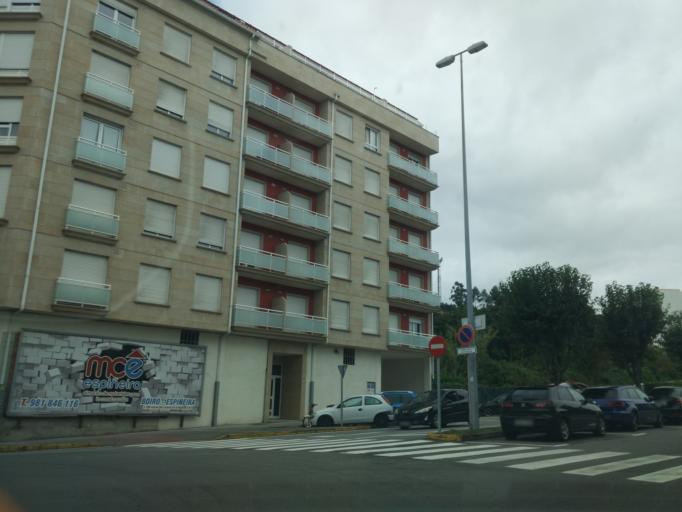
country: ES
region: Galicia
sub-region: Provincia da Coruna
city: Boiro
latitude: 42.6481
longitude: -8.8788
